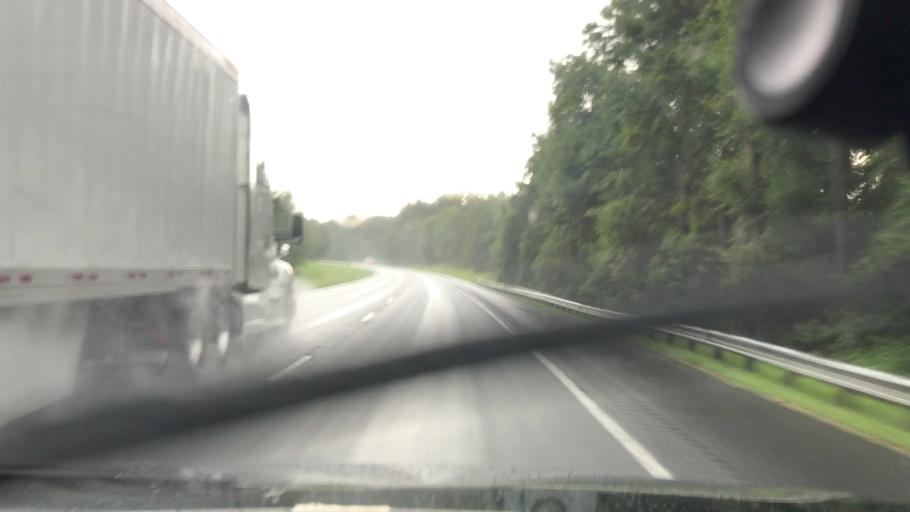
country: US
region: North Carolina
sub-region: Iredell County
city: Statesville
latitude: 35.9770
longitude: -80.8377
